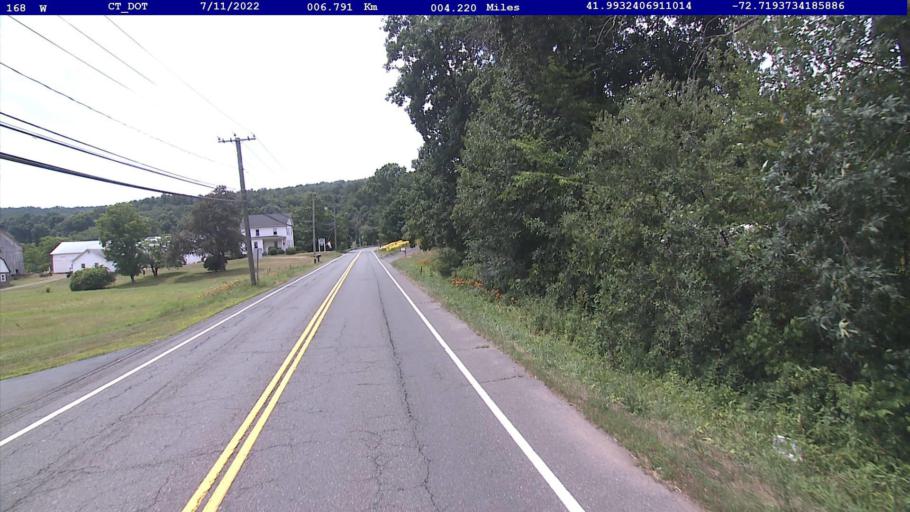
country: US
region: Connecticut
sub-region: Hartford County
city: Suffield Depot
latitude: 41.9930
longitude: -72.7193
